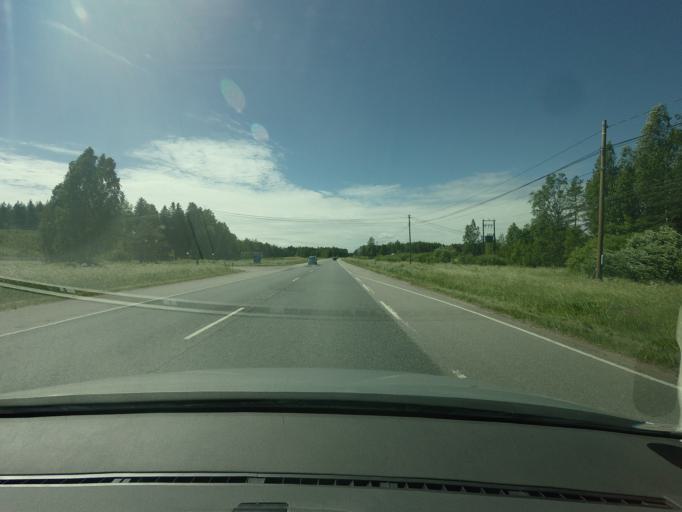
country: FI
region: Uusimaa
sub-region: Helsinki
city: Siuntio
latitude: 60.0942
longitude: 24.2408
